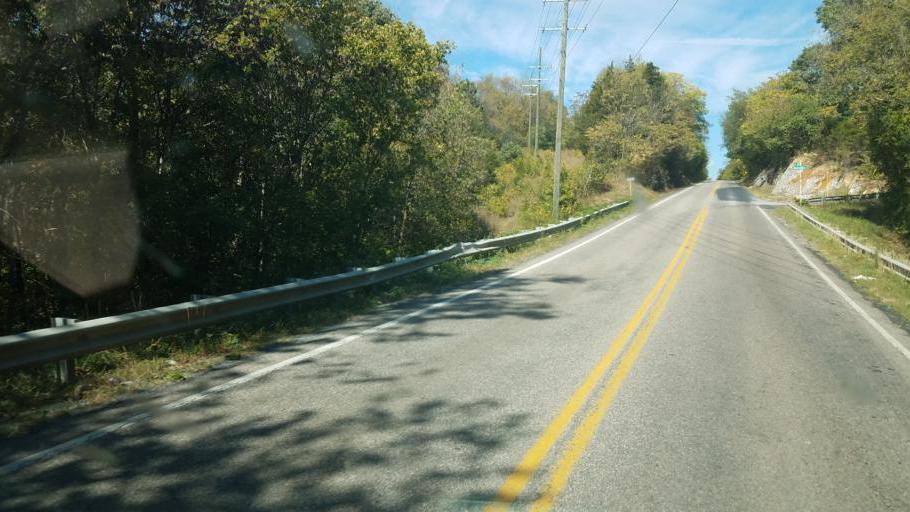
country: US
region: Virginia
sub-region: Page County
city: Shenandoah
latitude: 38.5165
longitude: -78.6170
